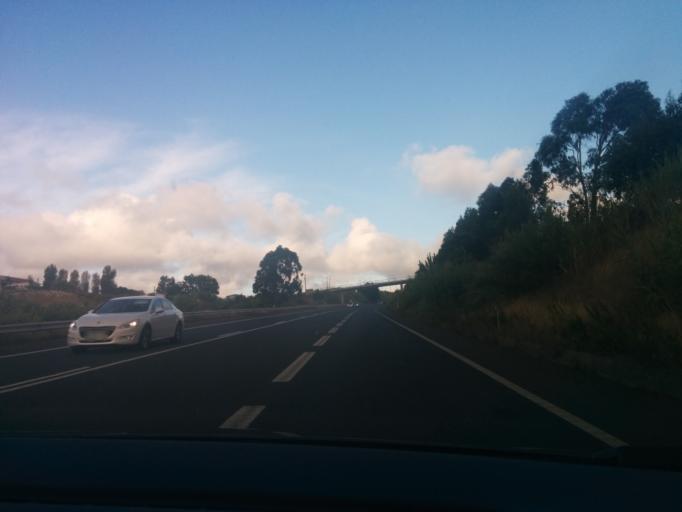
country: PT
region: Leiria
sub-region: Peniche
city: Atouguia da Baleia
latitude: 39.3264
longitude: -9.2913
